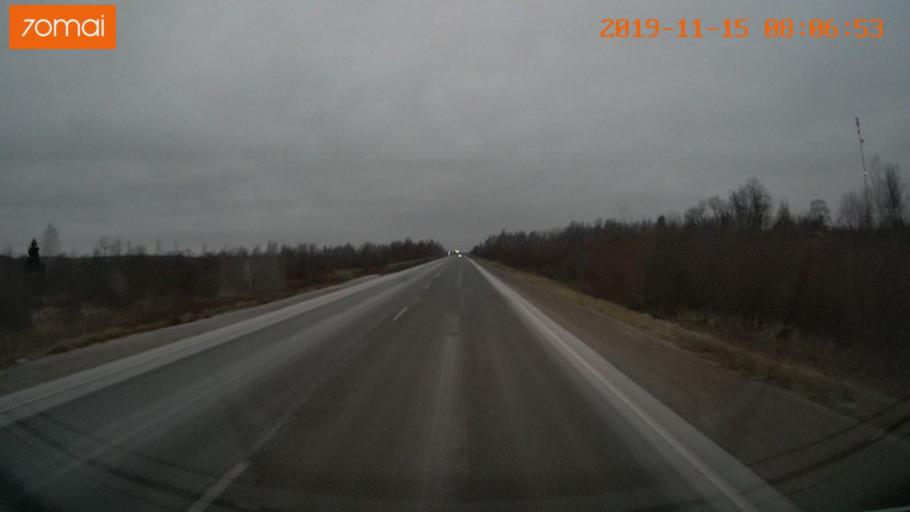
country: RU
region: Vologda
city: Cherepovets
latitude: 59.0241
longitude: 38.0281
